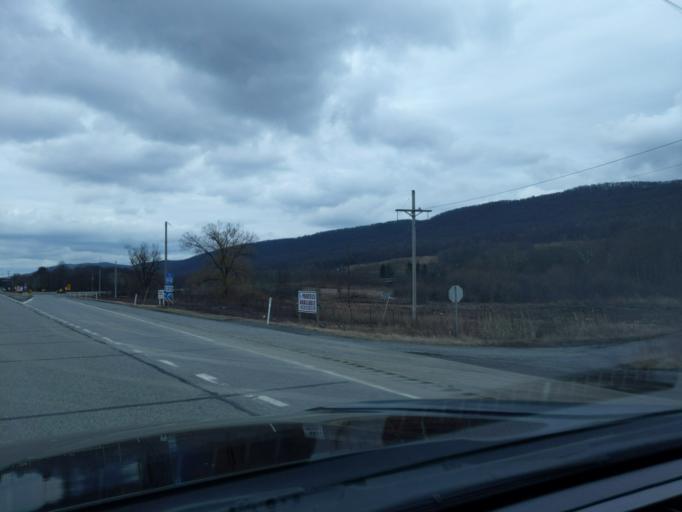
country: US
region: Pennsylvania
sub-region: Blair County
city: Tipton
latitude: 40.6421
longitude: -78.2782
